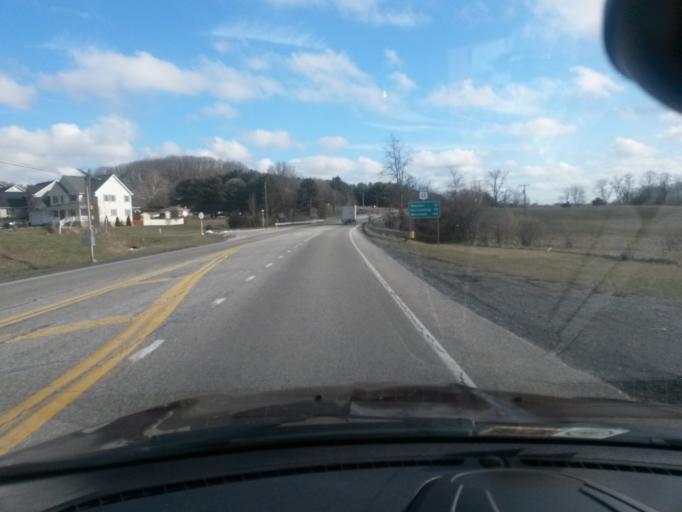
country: US
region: Virginia
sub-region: Augusta County
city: Jolivue
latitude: 38.0329
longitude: -79.1378
